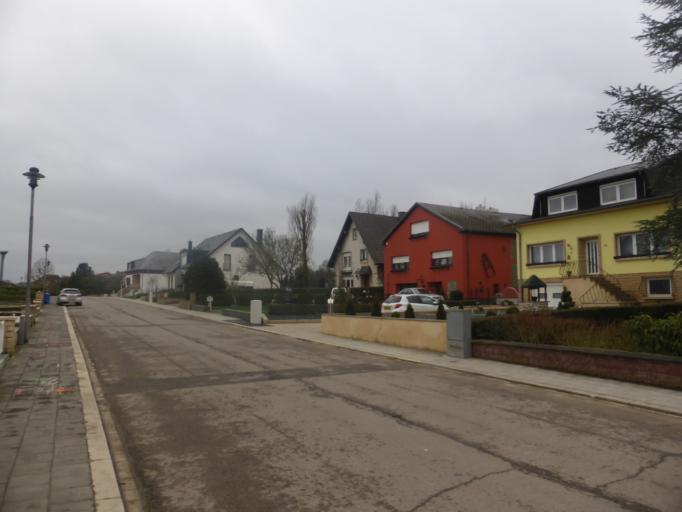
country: LU
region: Luxembourg
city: Bergem
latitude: 49.5289
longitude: 6.0419
